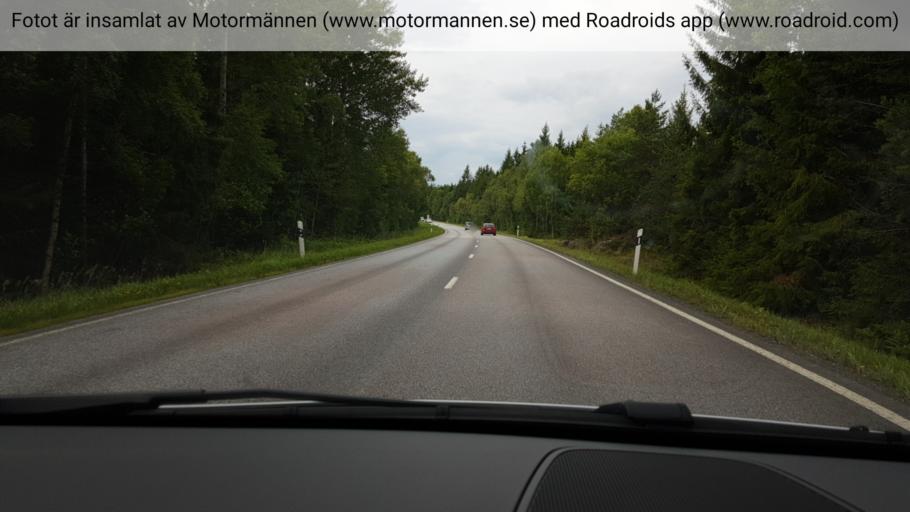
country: SE
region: Uppsala
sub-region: Osthammars Kommun
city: Oregrund
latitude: 60.3302
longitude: 18.3922
